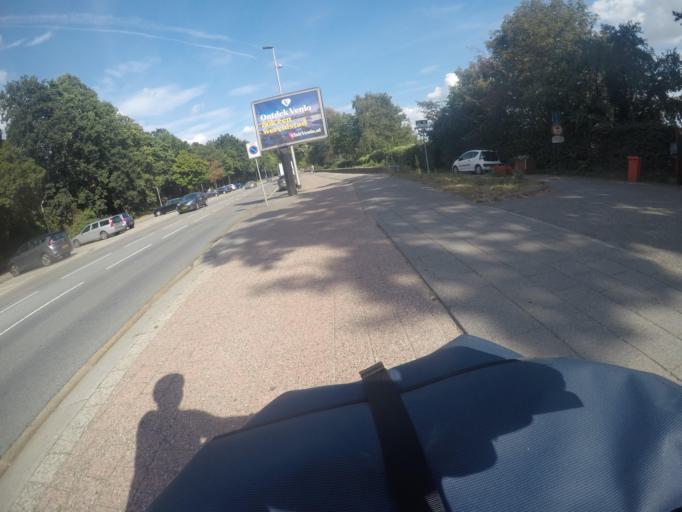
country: NL
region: Gelderland
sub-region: Gemeente Arnhem
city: Sterrenberg
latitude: 51.9840
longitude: 5.8859
